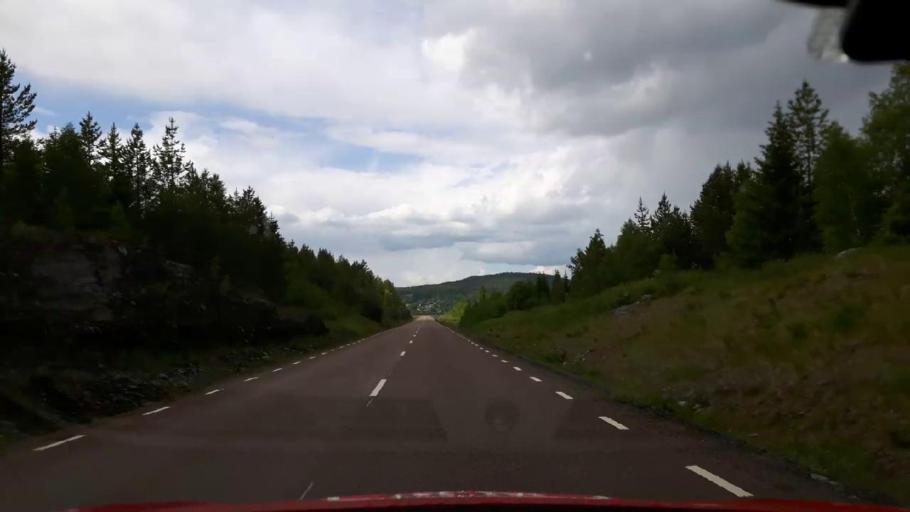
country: SE
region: Jaemtland
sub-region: Krokoms Kommun
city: Valla
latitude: 63.8960
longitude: 14.2545
